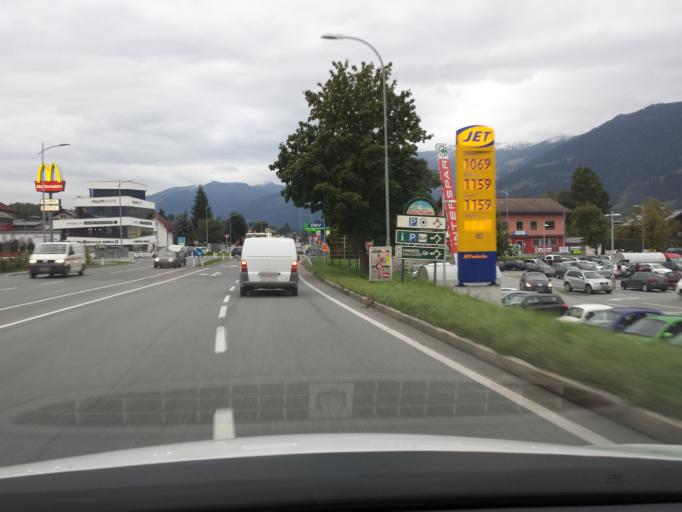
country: AT
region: Salzburg
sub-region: Politischer Bezirk Zell am See
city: Saalfelden am Steinernen Meer
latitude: 47.4297
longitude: 12.8437
